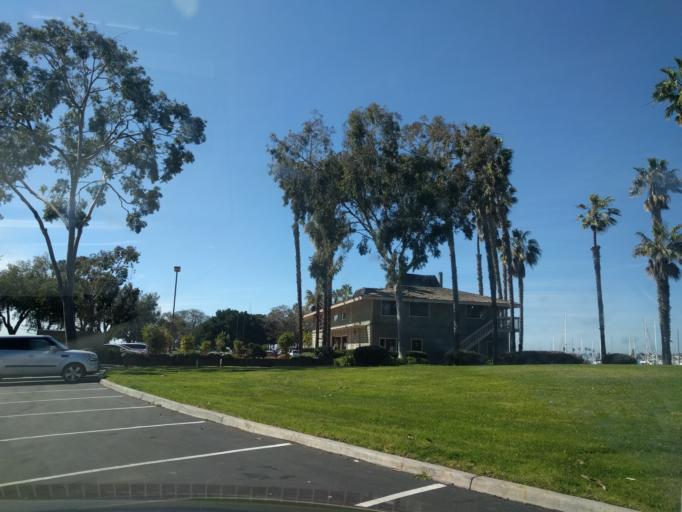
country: US
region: California
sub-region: San Diego County
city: San Diego
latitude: 32.7598
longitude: -117.2339
